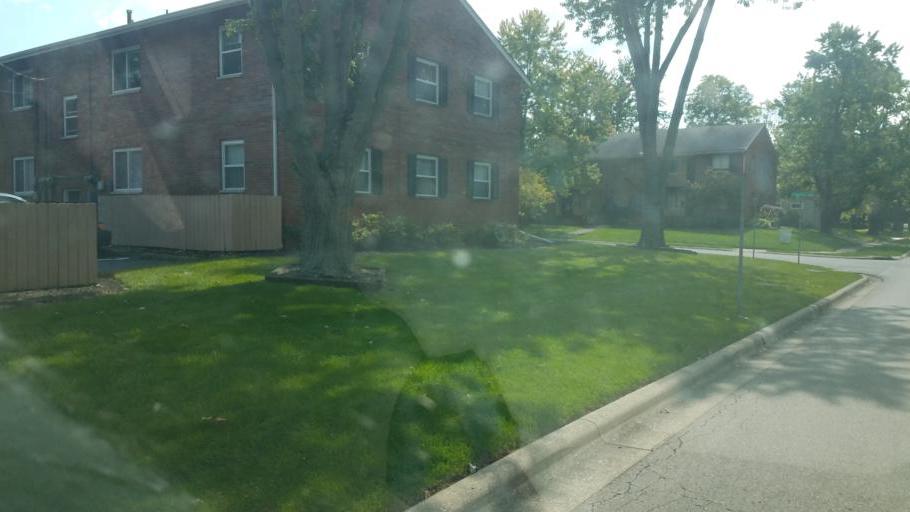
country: US
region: Ohio
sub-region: Franklin County
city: Worthington
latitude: 40.0923
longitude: -83.0137
